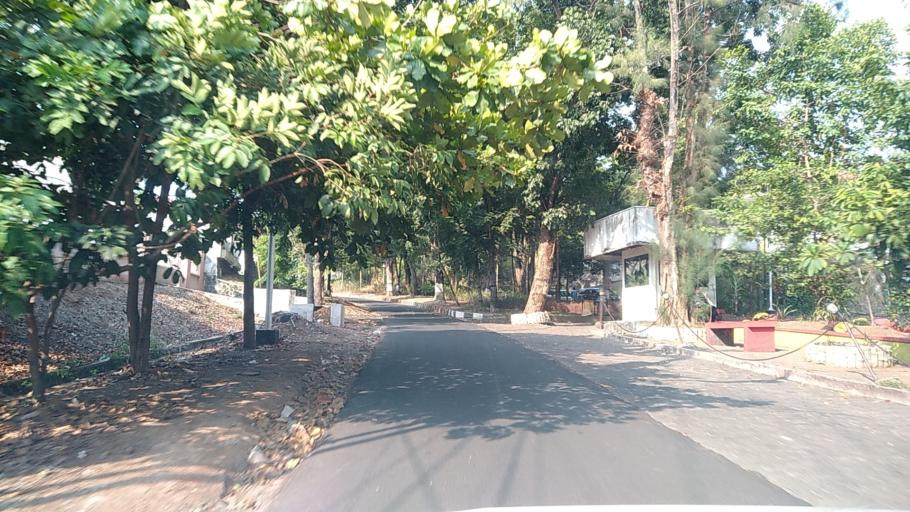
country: ID
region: Central Java
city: Semarang
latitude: -7.0090
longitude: 110.4130
